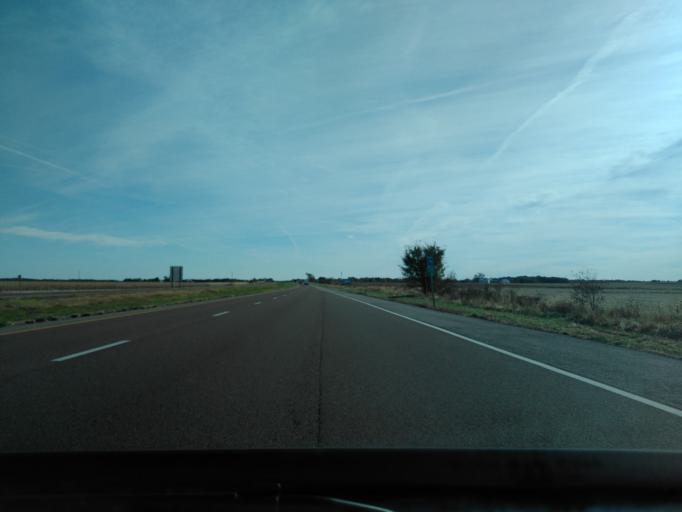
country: US
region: Illinois
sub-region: Madison County
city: Saint Jacob
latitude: 38.7620
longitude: -89.7961
